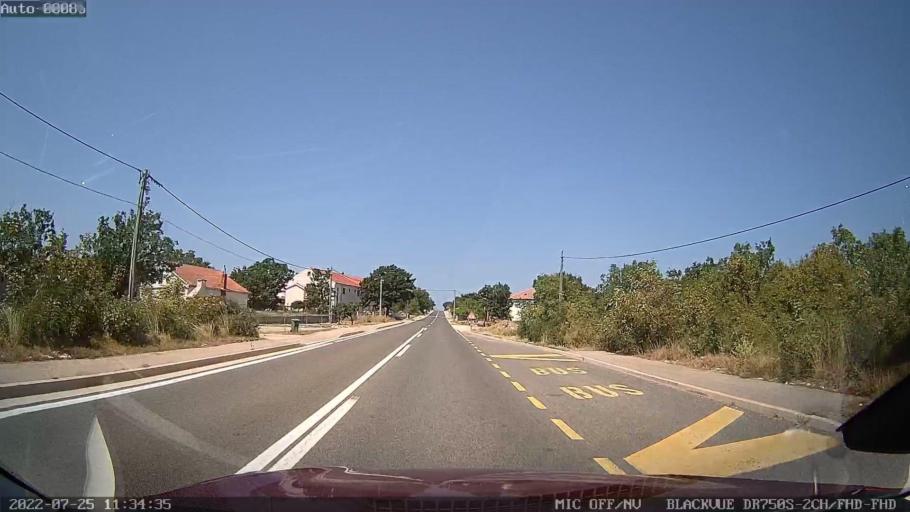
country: HR
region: Zadarska
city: Posedarje
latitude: 44.2304
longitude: 15.4201
